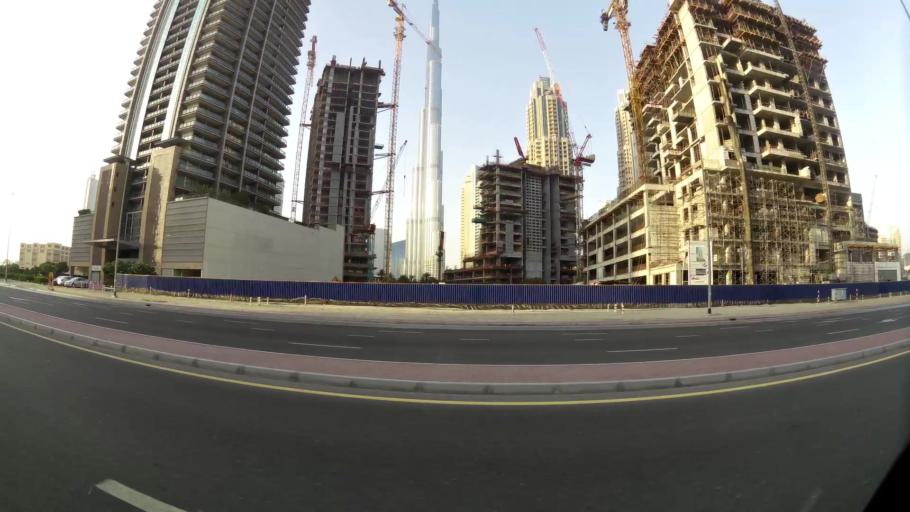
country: AE
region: Dubai
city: Dubai
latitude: 25.1899
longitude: 55.2702
